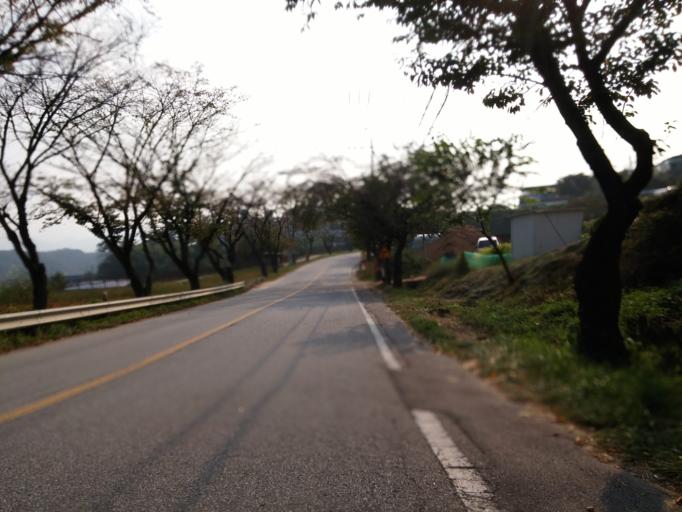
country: KR
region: Chungcheongbuk-do
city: Okcheon
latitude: 36.3199
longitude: 127.5820
